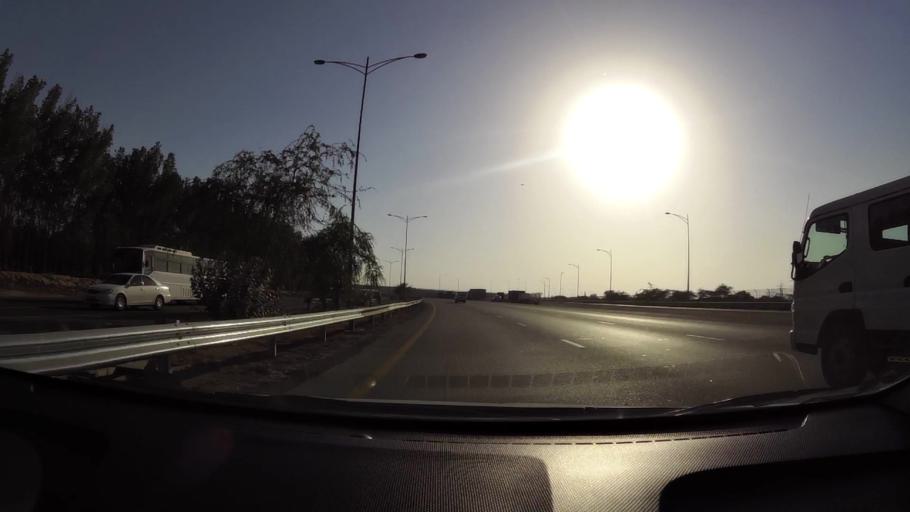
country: AE
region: Ajman
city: Ajman
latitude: 25.3591
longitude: 55.4859
